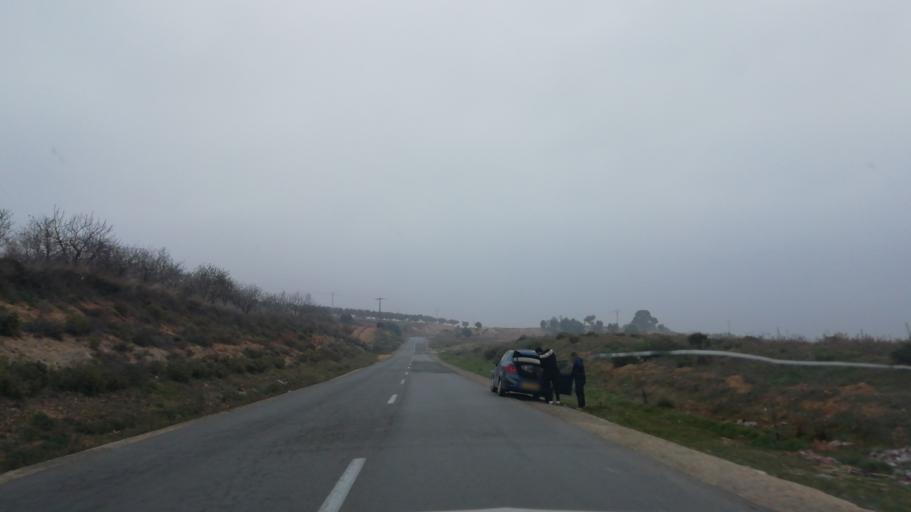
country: DZ
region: Mascara
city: Mascara
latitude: 35.4134
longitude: 0.1538
